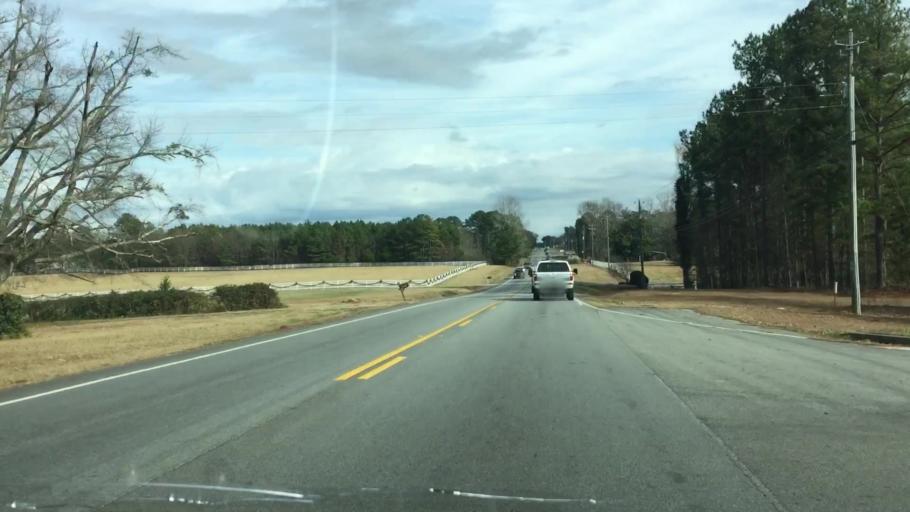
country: US
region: Georgia
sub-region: Henry County
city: McDonough
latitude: 33.4278
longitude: -84.0736
